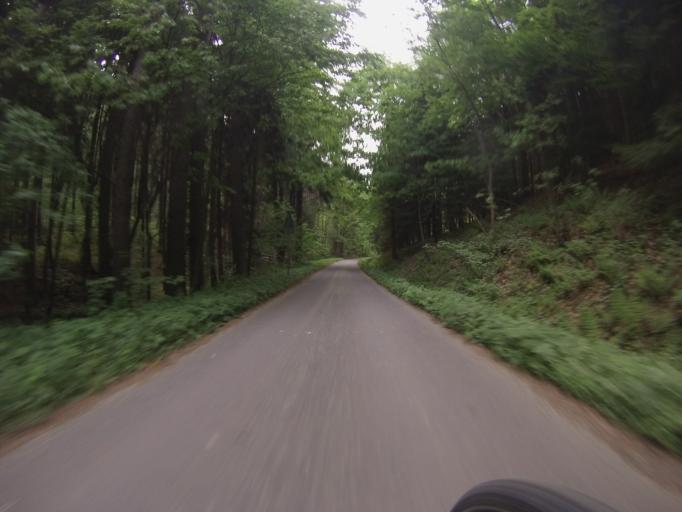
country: CZ
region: Olomoucky
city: Protivanov
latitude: 49.4678
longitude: 16.8794
